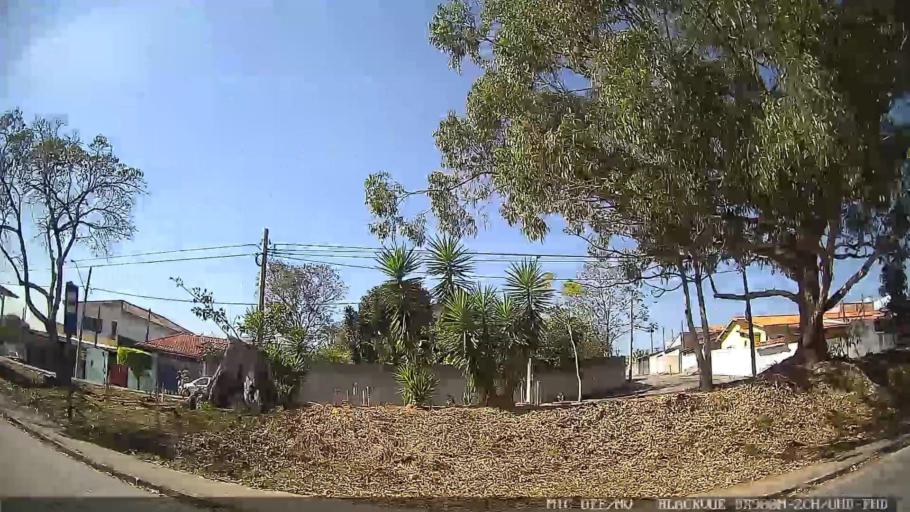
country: BR
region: Sao Paulo
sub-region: Jacarei
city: Jacarei
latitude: -23.3269
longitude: -45.9963
